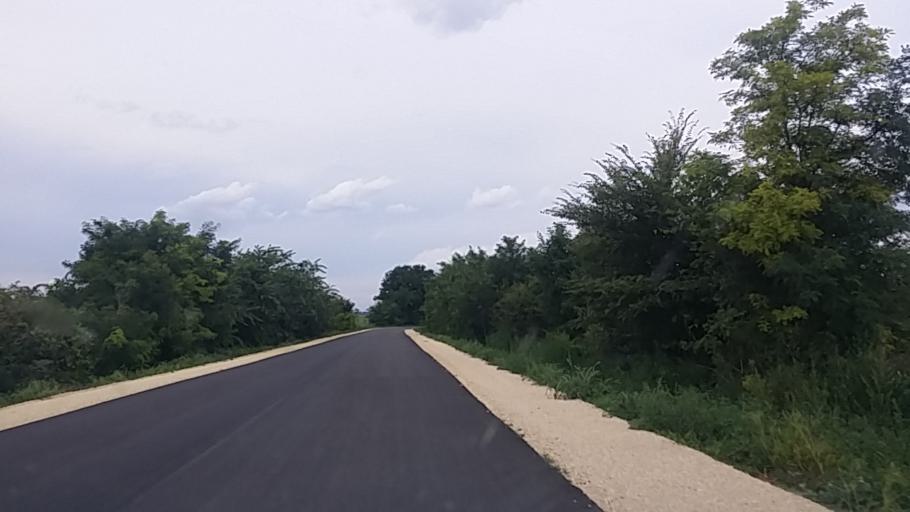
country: HU
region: Tolna
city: Tengelic
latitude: 46.5381
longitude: 18.6646
